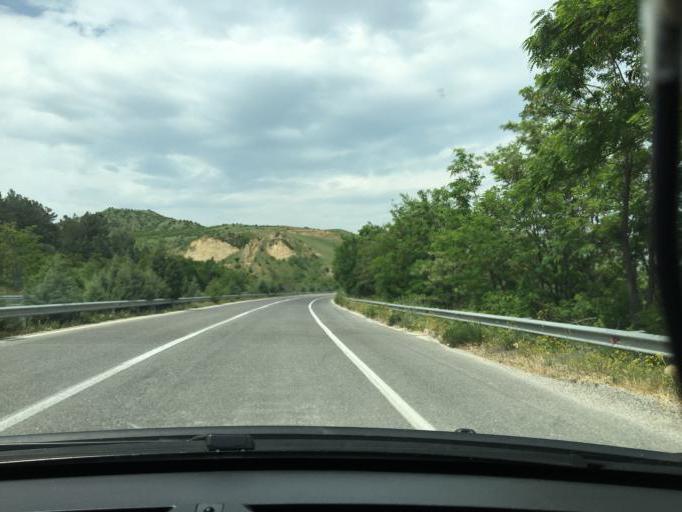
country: MK
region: Demir Kapija
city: Demir Kapija
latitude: 41.4169
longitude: 22.1986
